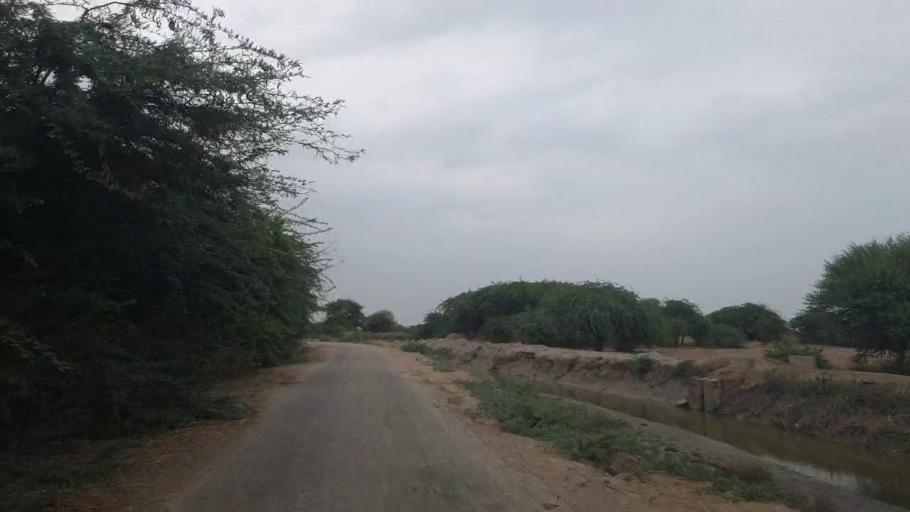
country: PK
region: Sindh
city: Badin
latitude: 24.6222
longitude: 68.6822
